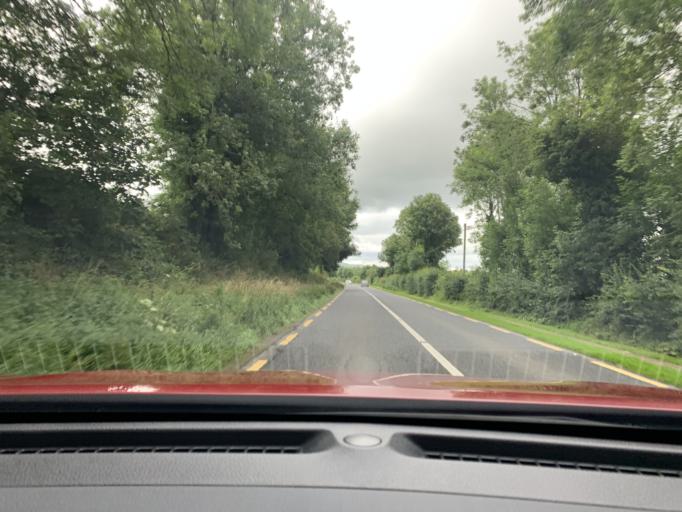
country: IE
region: Ulster
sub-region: County Donegal
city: Raphoe
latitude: 54.8027
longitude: -7.6089
